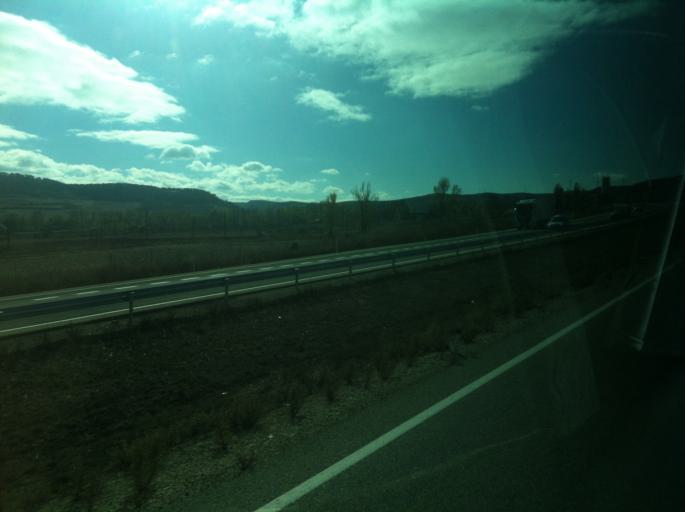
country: ES
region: Castille and Leon
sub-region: Provincia de Burgos
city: Santa Olalla de Bureba
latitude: 42.4705
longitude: -3.4455
